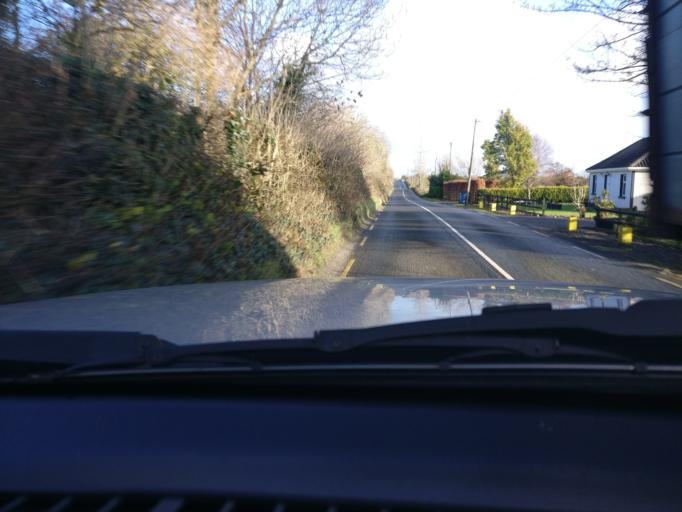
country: IE
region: Leinster
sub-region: An Iarmhi
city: Kilbeggan
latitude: 53.4698
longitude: -7.4809
